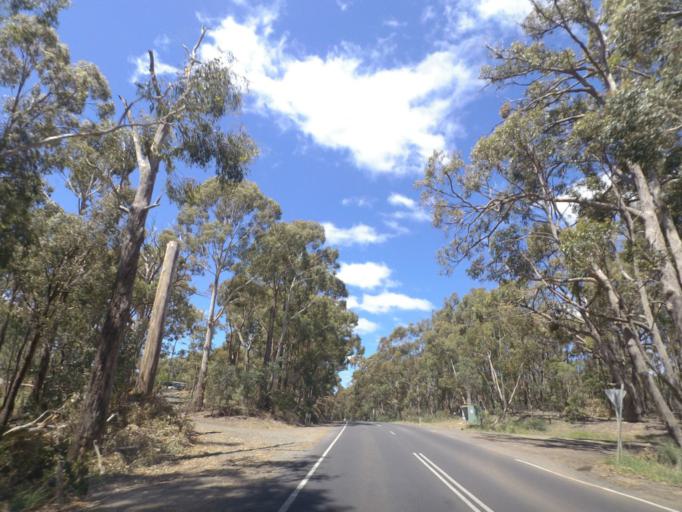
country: AU
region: Victoria
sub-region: Mount Alexander
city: Castlemaine
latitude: -37.2872
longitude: 144.2798
